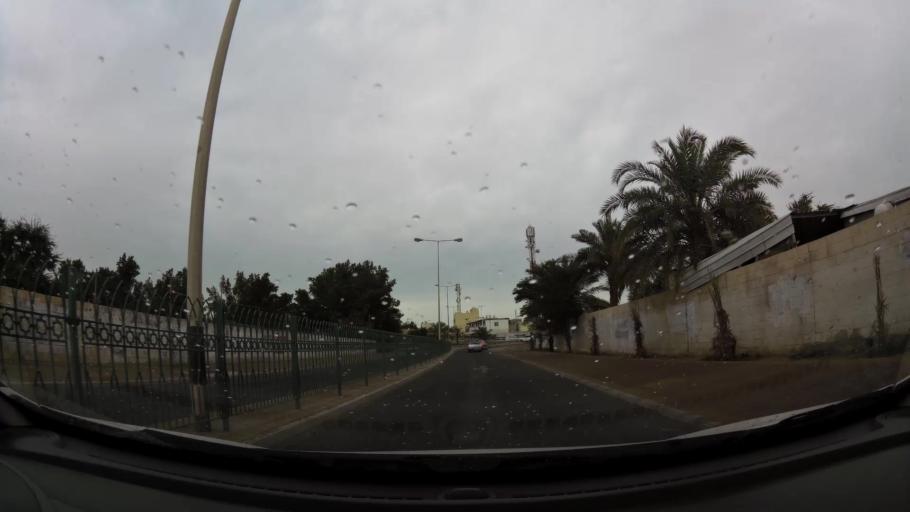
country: BH
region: Central Governorate
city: Madinat Hamad
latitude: 26.1116
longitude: 50.4823
